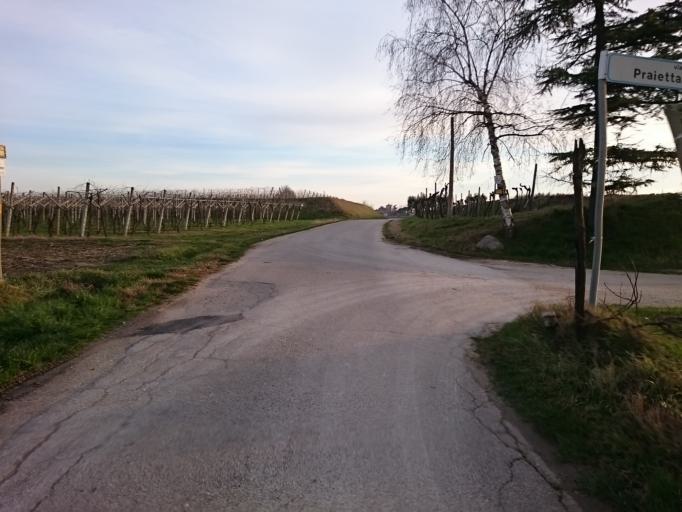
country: IT
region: Veneto
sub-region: Provincia di Verona
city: Castelnuovo del Garda
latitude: 45.4483
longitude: 10.7532
